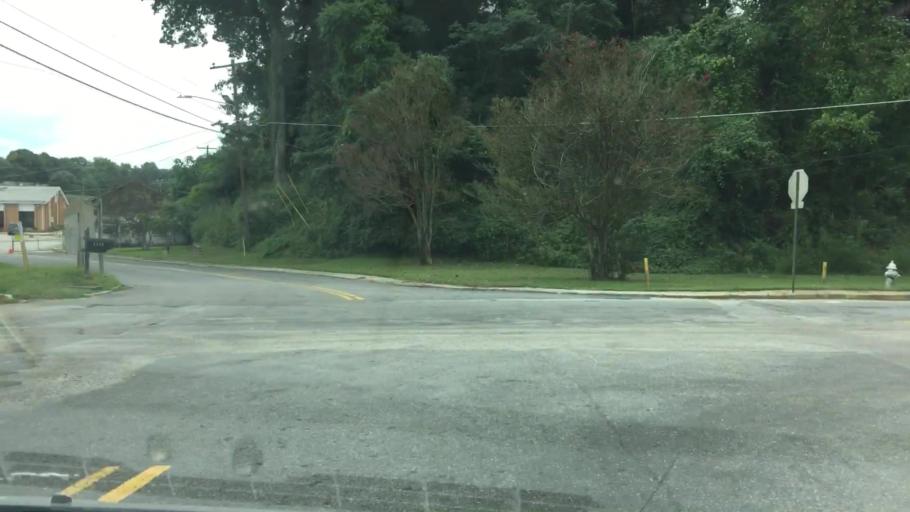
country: US
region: Georgia
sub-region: Fulton County
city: Atlanta
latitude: 33.7688
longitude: -84.4253
